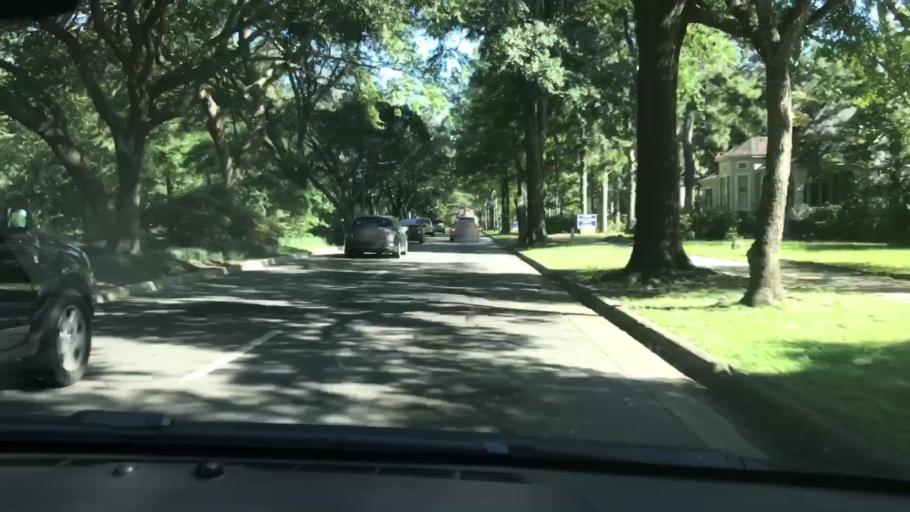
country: US
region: Alabama
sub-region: Barbour County
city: Eufaula
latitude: 31.8984
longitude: -85.1457
